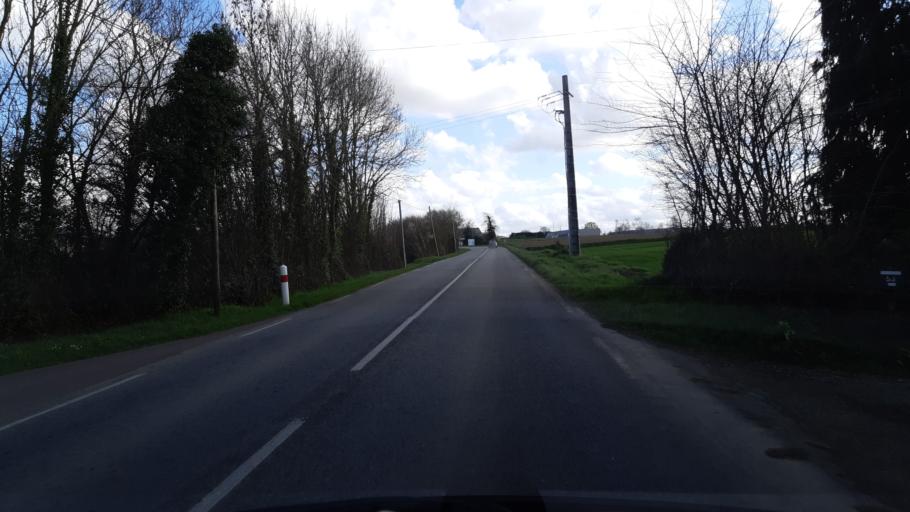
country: FR
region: Lower Normandy
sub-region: Departement de la Manche
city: Agneaux
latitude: 49.0568
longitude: -1.1328
